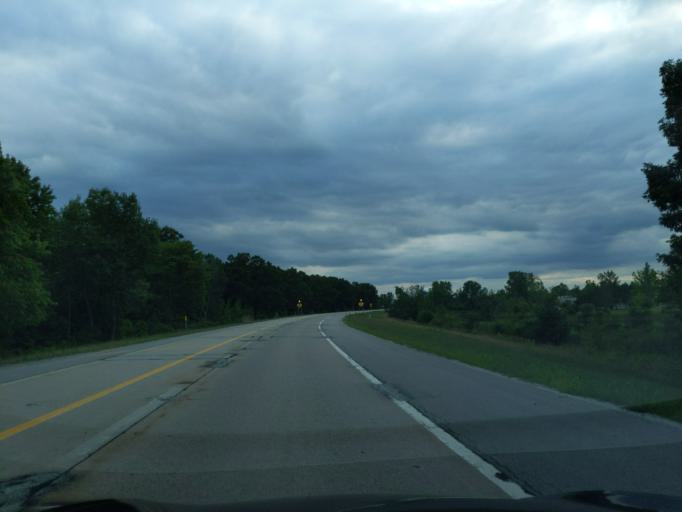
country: US
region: Michigan
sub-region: Isabella County
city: Mount Pleasant
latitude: 43.6227
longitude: -84.7598
